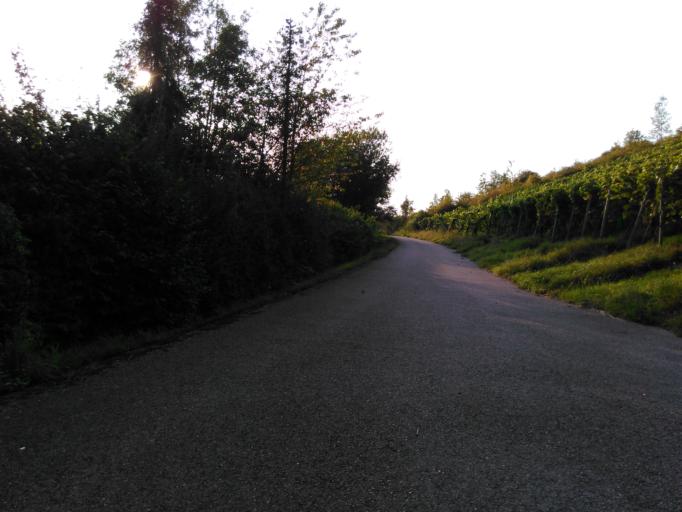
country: LU
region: Grevenmacher
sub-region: Canton de Remich
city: Lenningen
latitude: 49.6119
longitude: 6.3747
